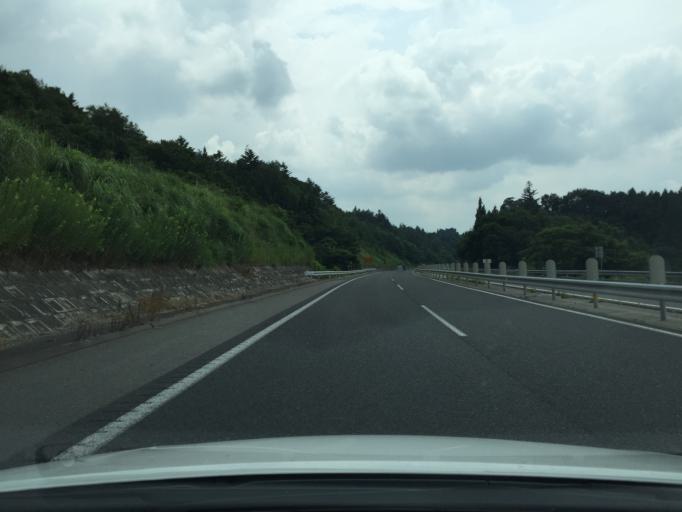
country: JP
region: Fukushima
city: Funehikimachi-funehiki
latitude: 37.3264
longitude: 140.6175
